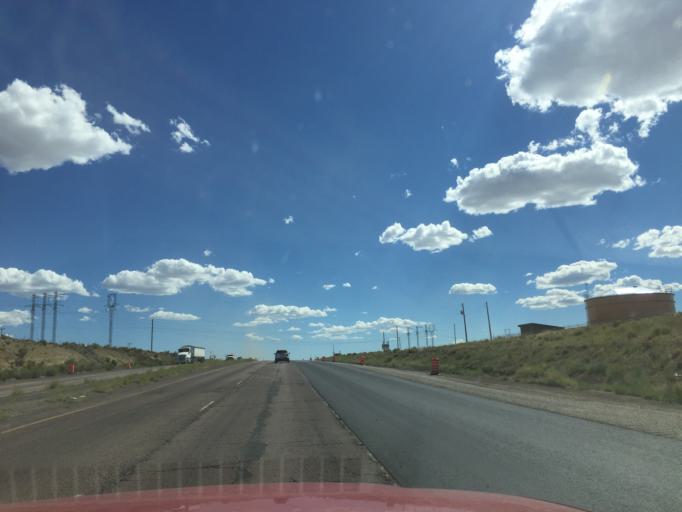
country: US
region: New Mexico
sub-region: McKinley County
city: Twin Lakes
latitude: 35.6470
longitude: -108.7726
